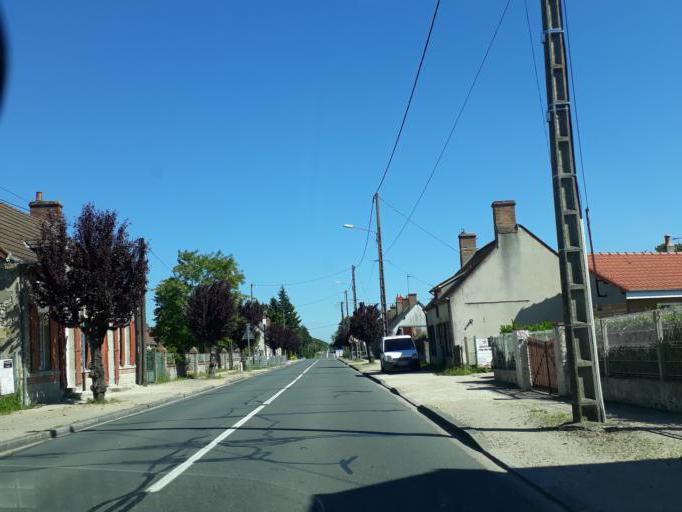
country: FR
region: Centre
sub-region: Departement du Loiret
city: Bray-en-Val
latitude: 47.8116
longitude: 2.4058
